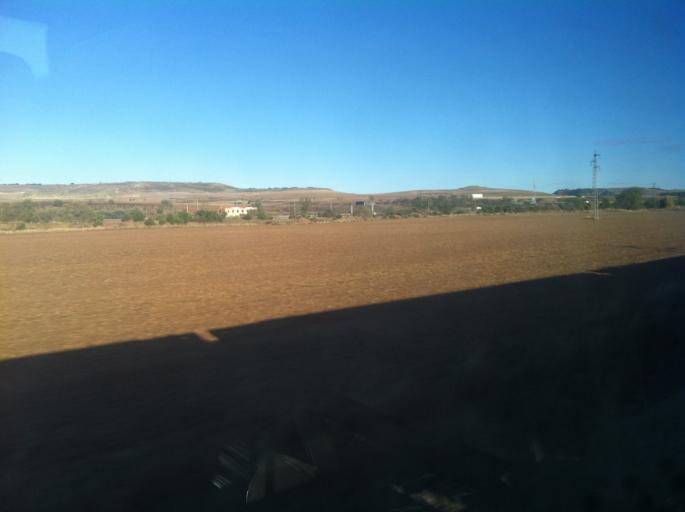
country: ES
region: Castille and Leon
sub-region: Provincia de Palencia
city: Duenas
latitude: 41.8485
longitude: -4.5551
